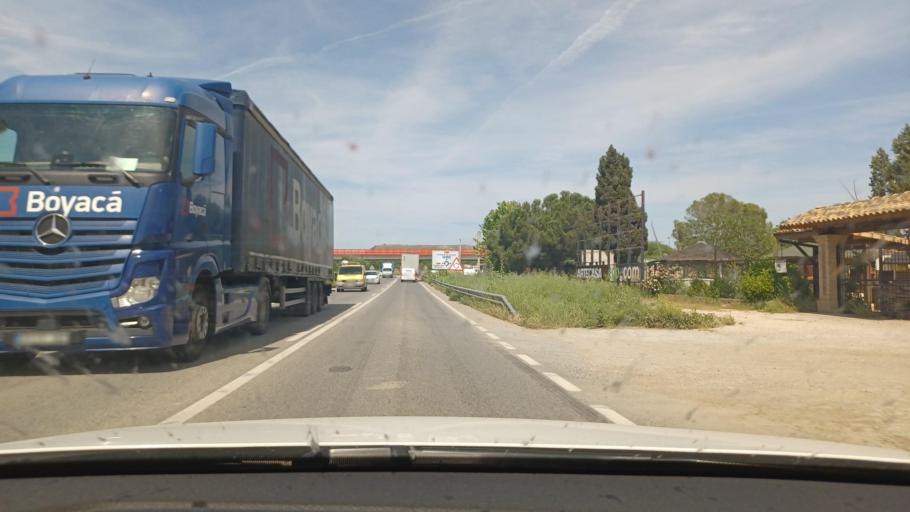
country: ES
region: Madrid
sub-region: Provincia de Madrid
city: Torrejon de Ardoz
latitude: 40.4290
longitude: -3.4474
